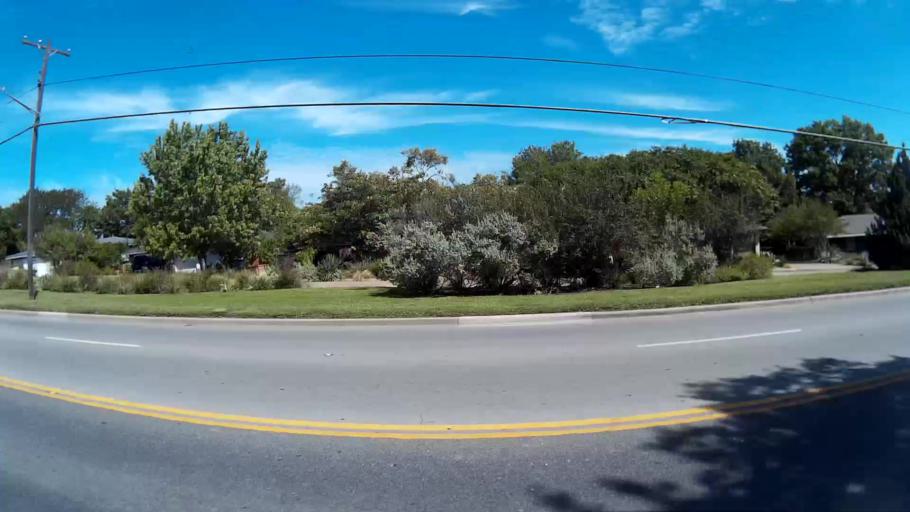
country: US
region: Texas
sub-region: Dallas County
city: Highland Park
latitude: 32.8145
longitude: -96.7356
